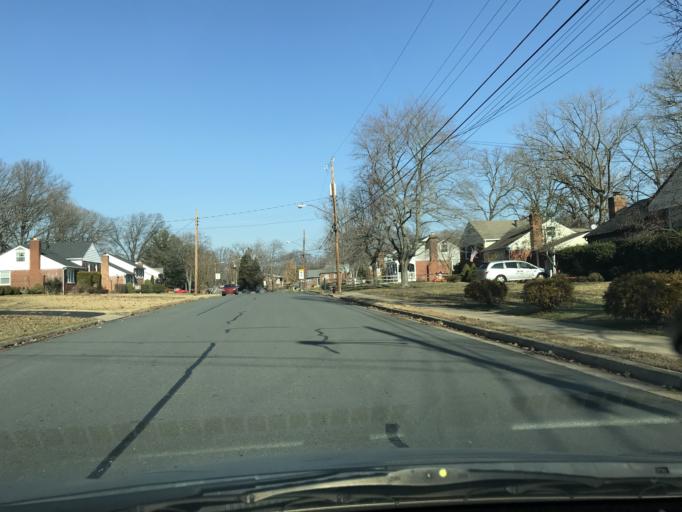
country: US
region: Virginia
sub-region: City of Fairfax
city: Fairfax
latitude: 38.8572
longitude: -77.3271
